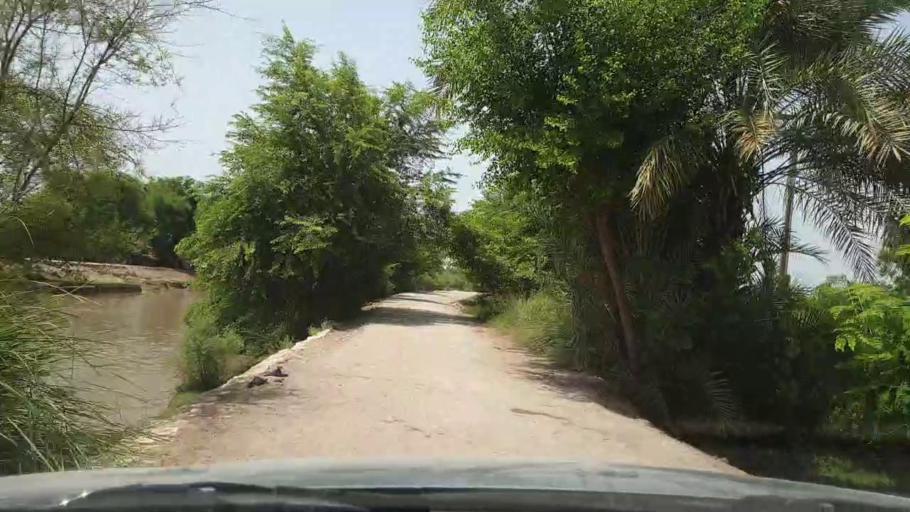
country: PK
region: Sindh
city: Pano Aqil
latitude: 27.9185
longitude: 69.1594
